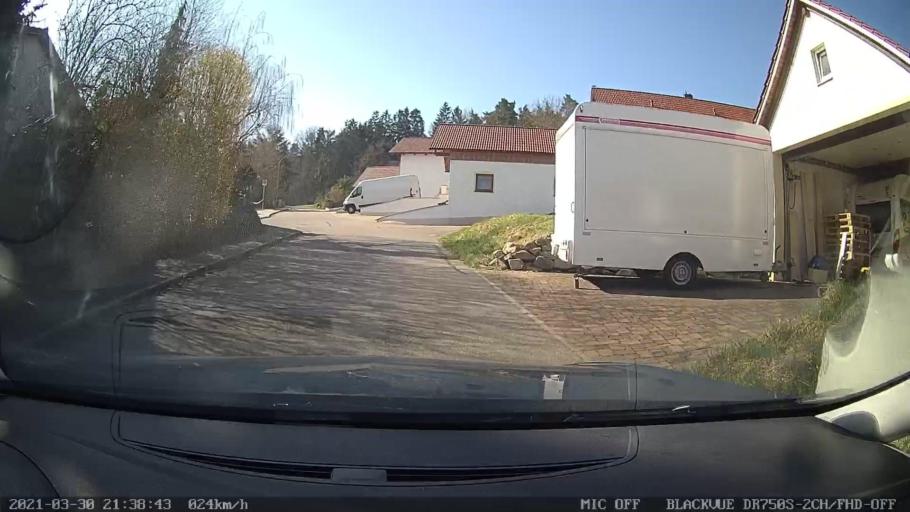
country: DE
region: Bavaria
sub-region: Upper Palatinate
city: Zeitlarn
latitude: 49.0984
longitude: 12.0999
